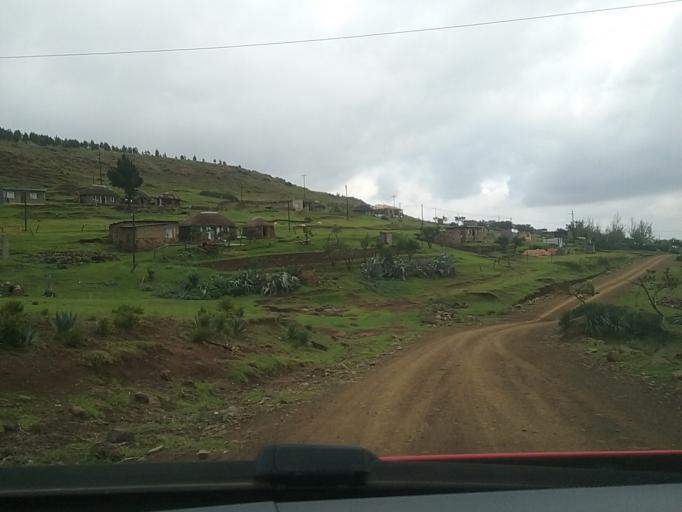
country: LS
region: Berea
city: Teyateyaneng
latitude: -29.2474
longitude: 27.8418
